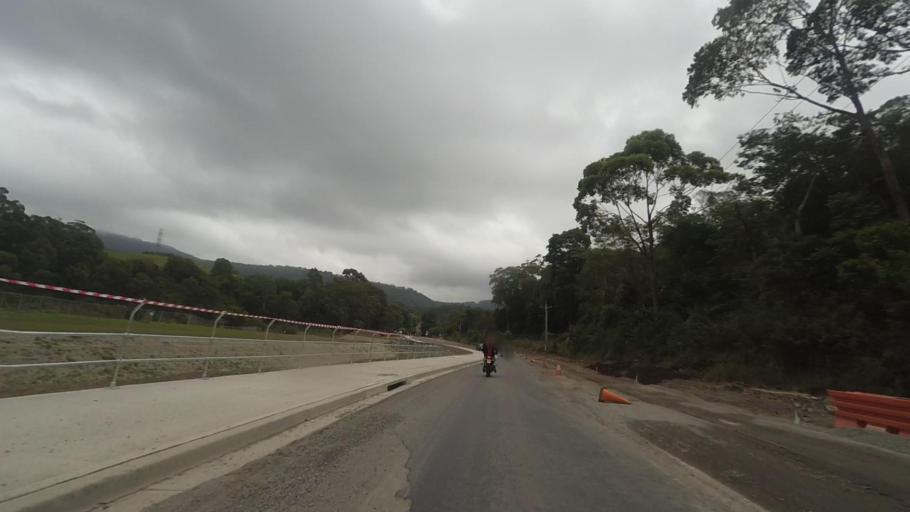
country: AU
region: New South Wales
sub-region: Wollongong
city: Cordeaux Heights
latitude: -34.4332
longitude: 150.8309
